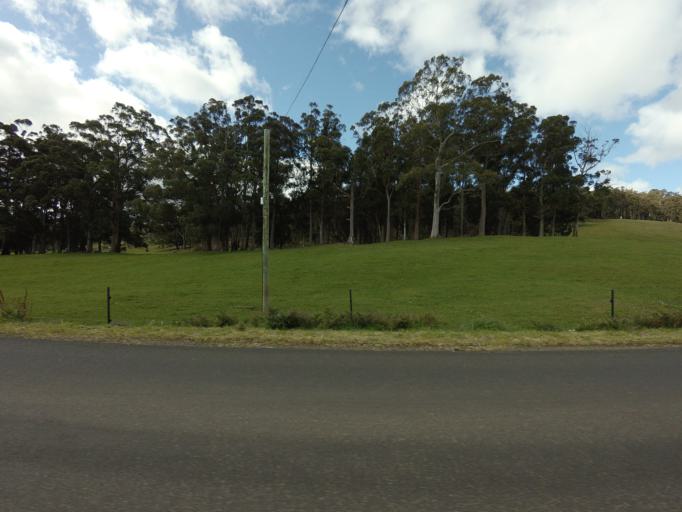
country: AU
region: Tasmania
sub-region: Huon Valley
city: Geeveston
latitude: -43.1817
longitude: 146.9282
